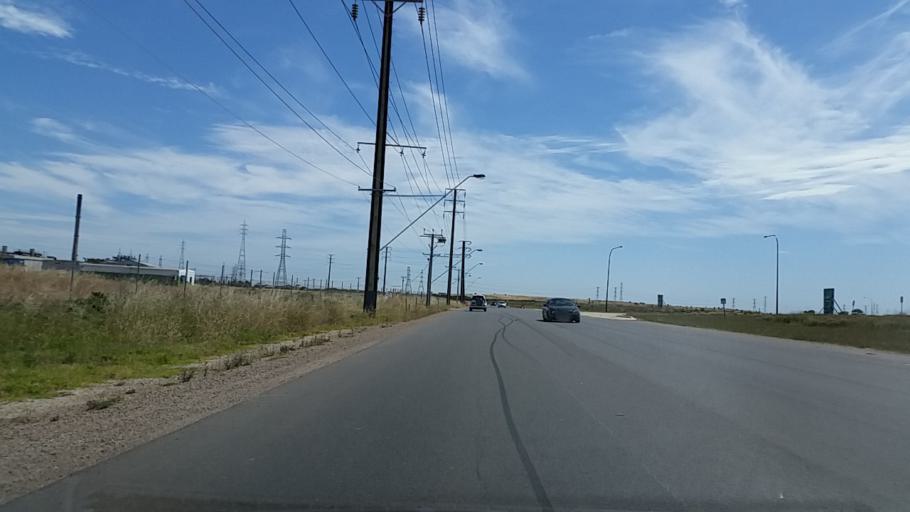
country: AU
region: South Australia
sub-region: Port Adelaide Enfield
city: Birkenhead
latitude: -34.8193
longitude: 138.5239
